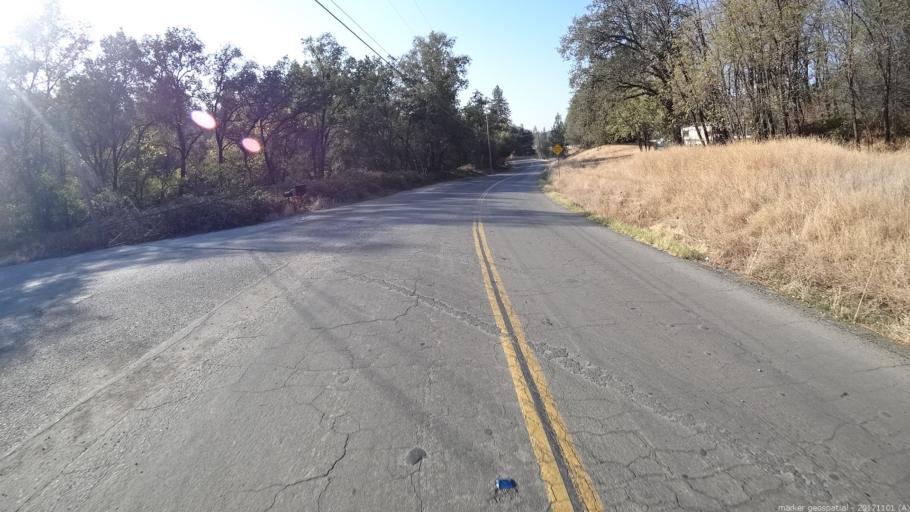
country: US
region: California
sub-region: Shasta County
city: Shasta Lake
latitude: 40.7341
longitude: -122.3169
